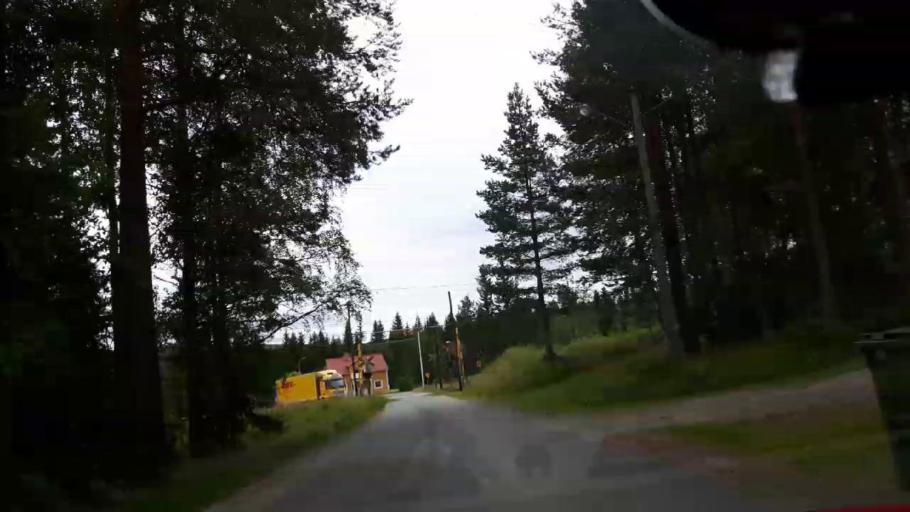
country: SE
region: Jaemtland
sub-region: Braecke Kommun
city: Braecke
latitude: 62.8896
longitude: 15.6092
